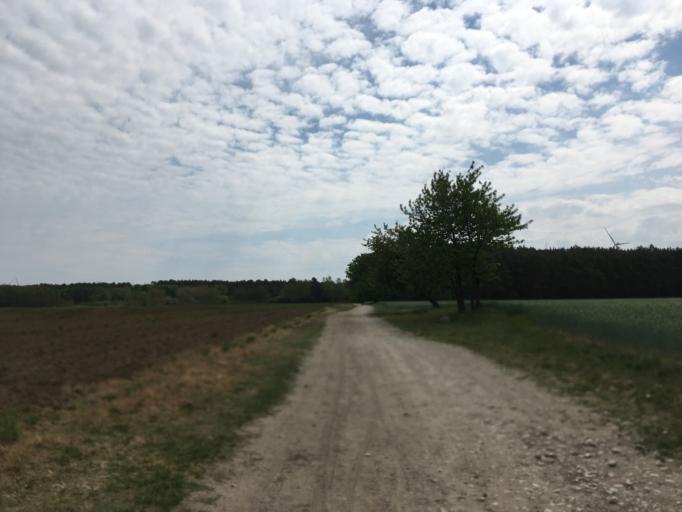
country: DE
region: Brandenburg
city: Rudnitz
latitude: 52.7136
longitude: 13.6233
